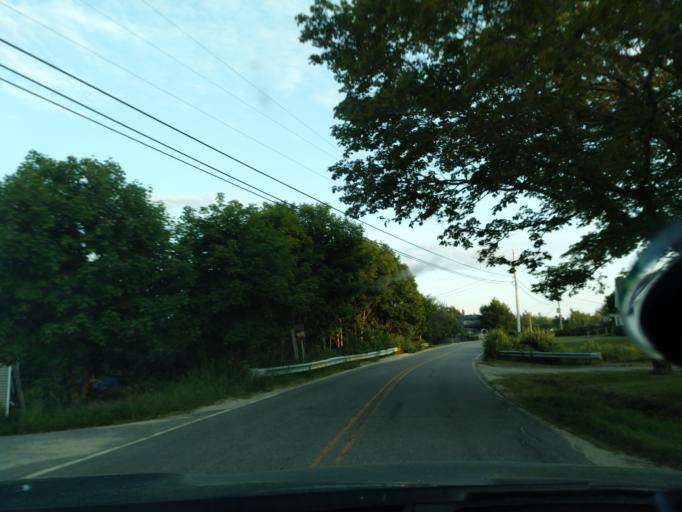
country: US
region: Maine
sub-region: Hancock County
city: Gouldsboro
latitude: 44.3882
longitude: -68.0394
